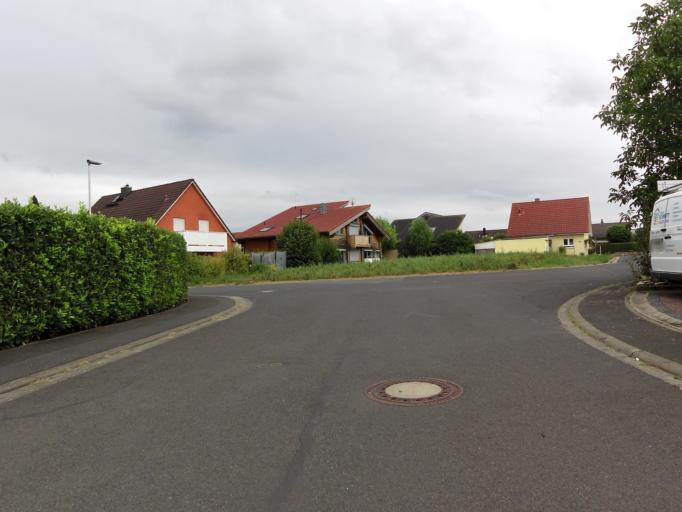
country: DE
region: Bavaria
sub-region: Regierungsbezirk Unterfranken
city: Rimpar
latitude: 49.8535
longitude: 9.9504
